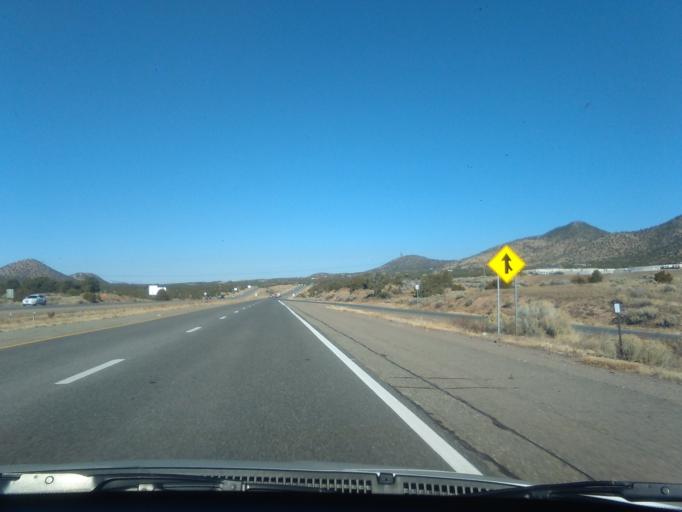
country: US
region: New Mexico
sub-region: Santa Fe County
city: Eldorado at Santa Fe
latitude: 35.5566
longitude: -105.8798
